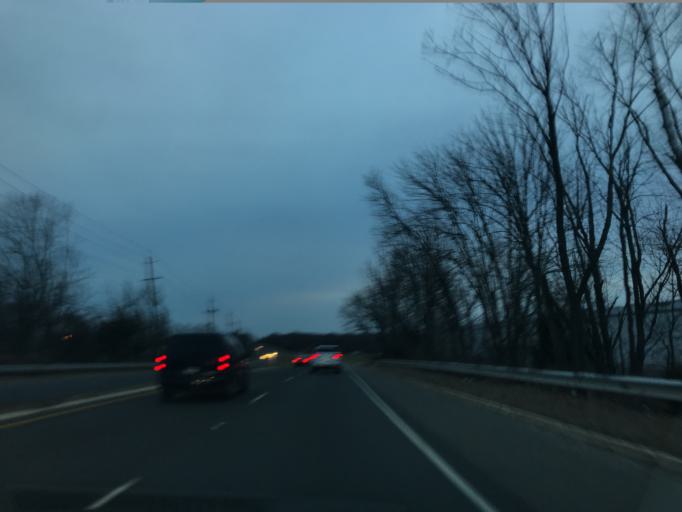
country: US
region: New Jersey
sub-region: Middlesex County
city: Dayton
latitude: 40.3733
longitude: -74.5006
